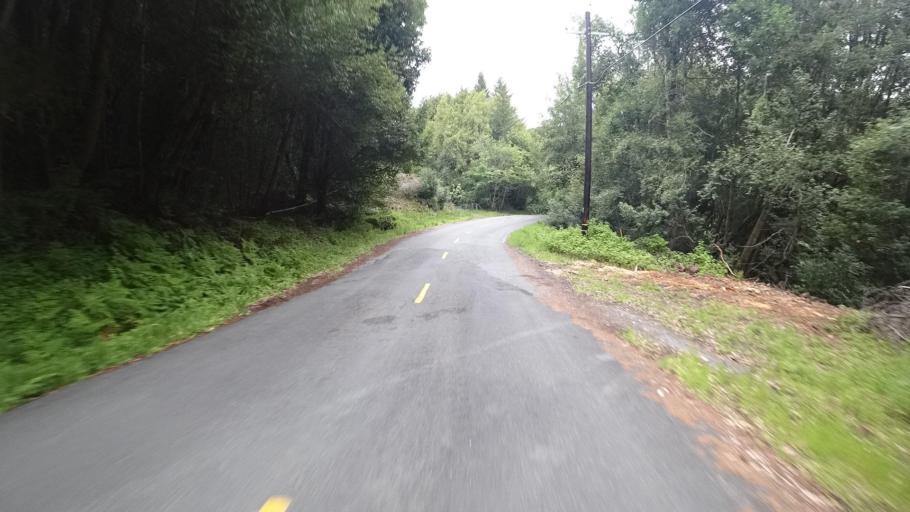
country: US
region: California
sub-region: Humboldt County
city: Blue Lake
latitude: 40.9489
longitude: -123.8412
